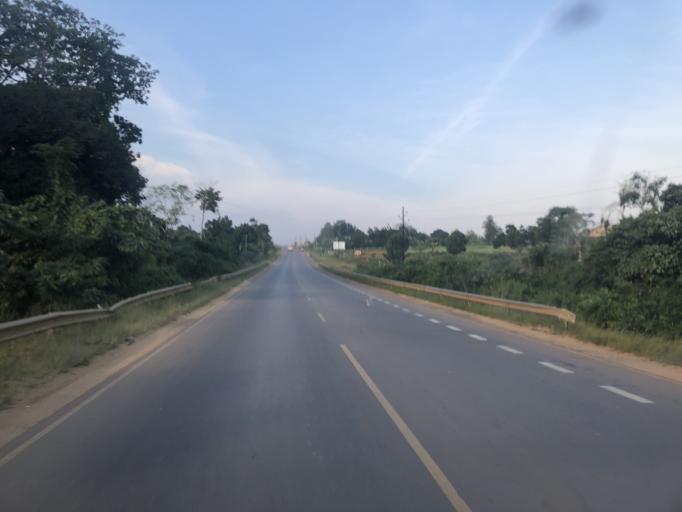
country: UG
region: Central Region
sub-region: Mpigi District
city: Mpigi
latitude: 0.2039
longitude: 32.3093
